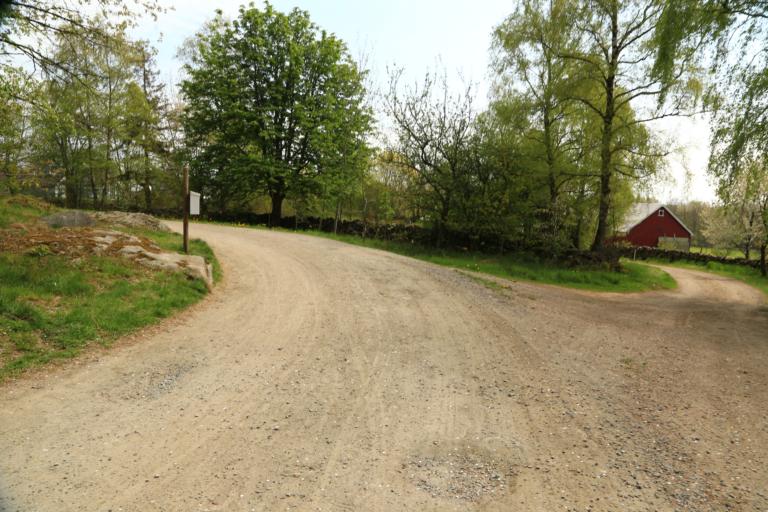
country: SE
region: Halland
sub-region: Varbergs Kommun
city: Varberg
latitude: 57.1354
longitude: 12.2921
